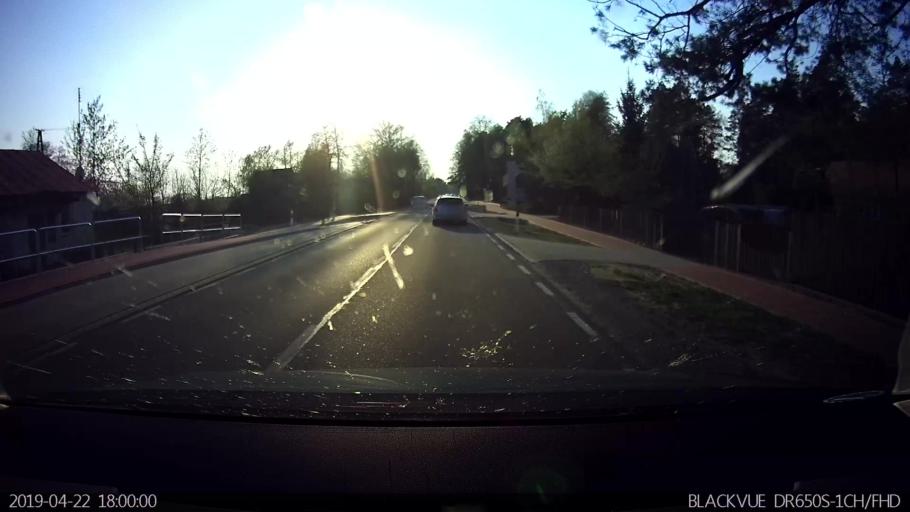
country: PL
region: Masovian Voivodeship
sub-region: Powiat wegrowski
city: Korytnica
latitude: 52.4751
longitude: 21.8528
